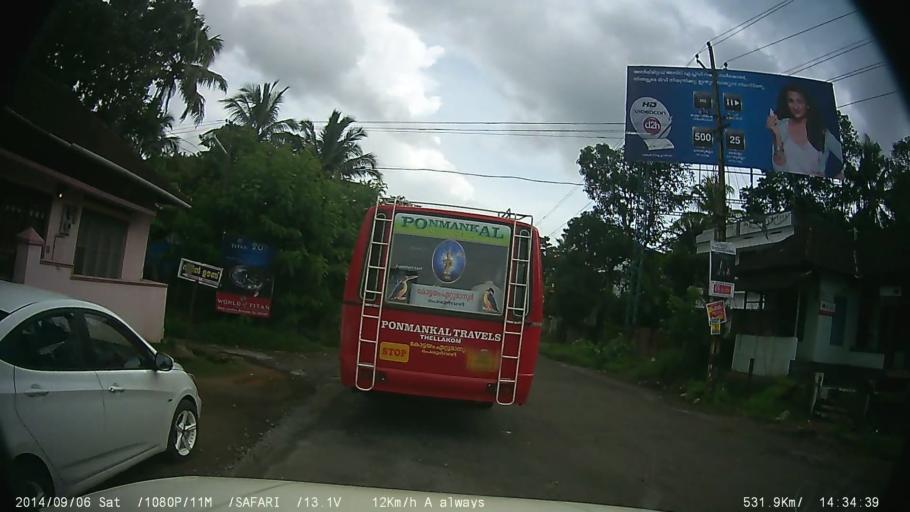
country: IN
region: Kerala
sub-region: Kottayam
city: Kottayam
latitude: 9.6048
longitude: 76.5321
